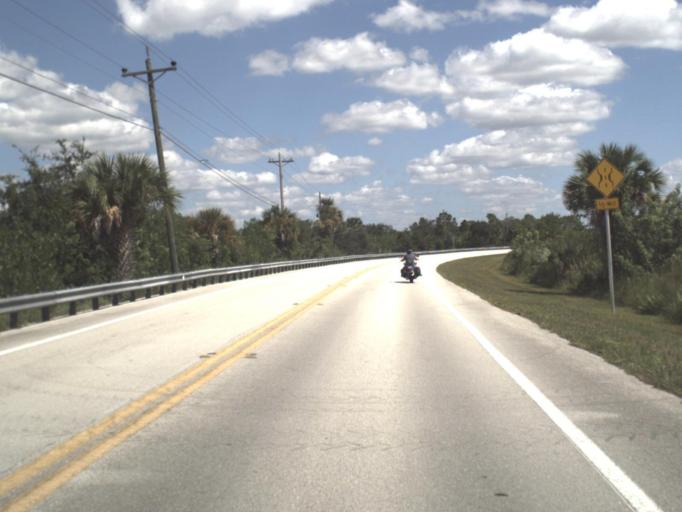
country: US
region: Florida
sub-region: Collier County
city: Marco
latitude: 25.9607
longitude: -81.4977
